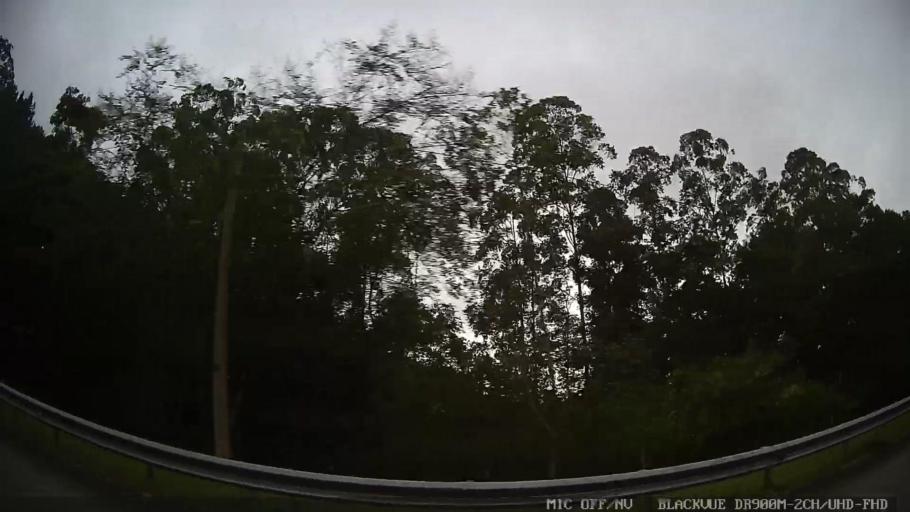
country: BR
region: Sao Paulo
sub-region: Caraguatatuba
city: Caraguatatuba
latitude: -23.5282
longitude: -45.5384
